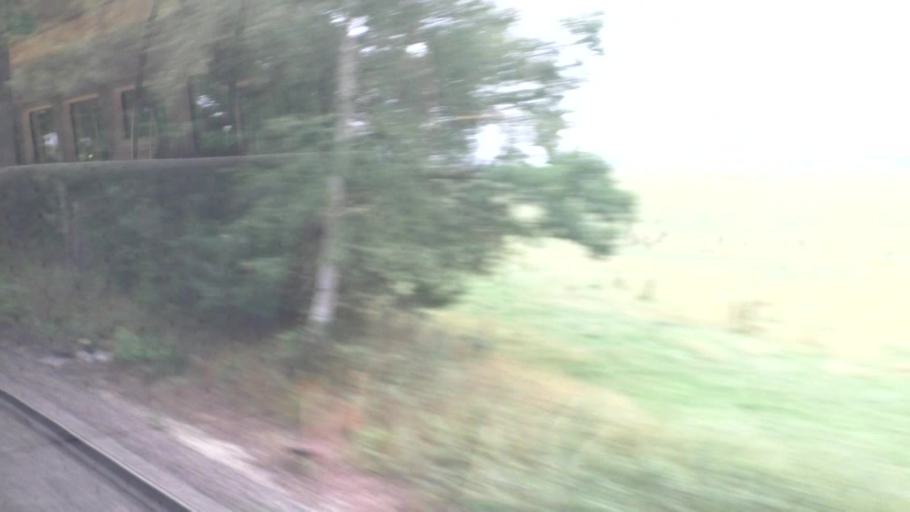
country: DE
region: Saxony
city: Bischofswerda
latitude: 51.1139
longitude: 14.1582
